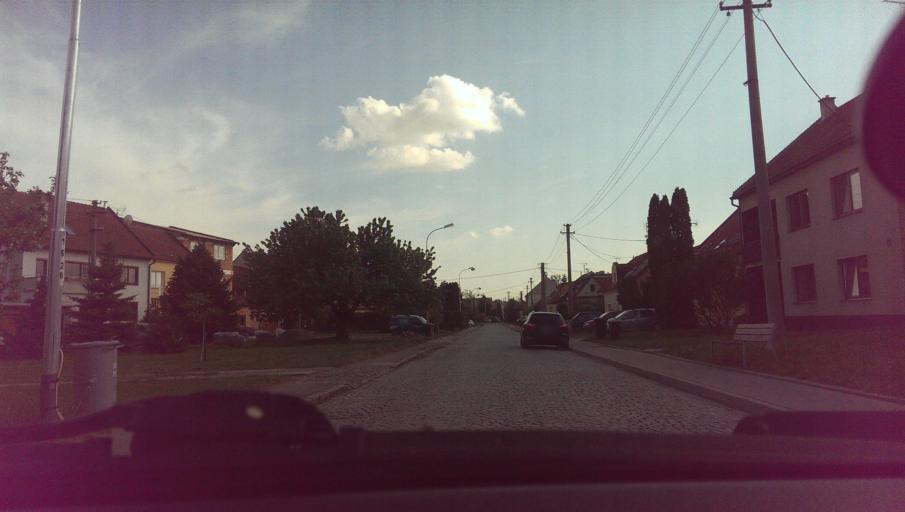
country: CZ
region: Zlin
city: Uhersky Brod
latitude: 49.0195
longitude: 17.6450
